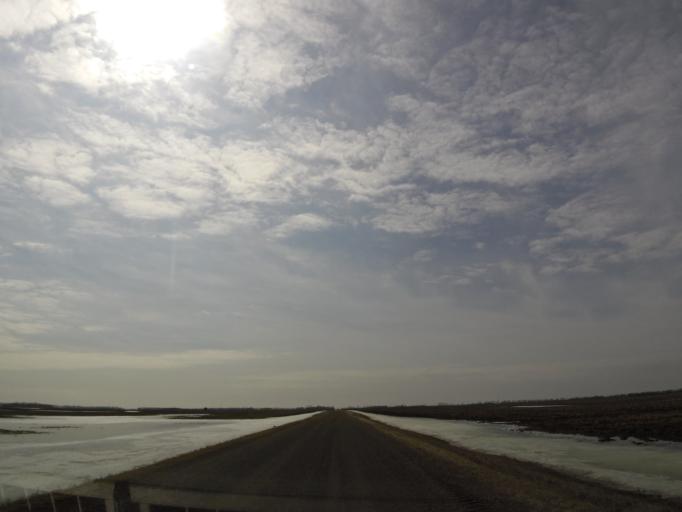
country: US
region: North Dakota
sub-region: Walsh County
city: Grafton
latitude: 48.3446
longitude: -97.2112
